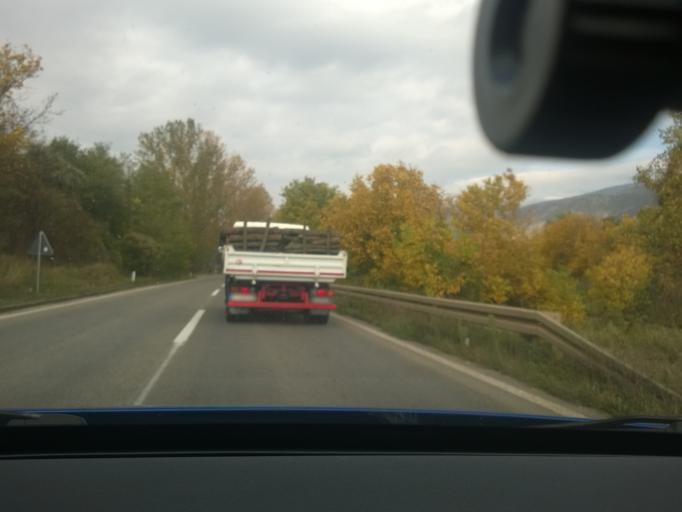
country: RS
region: Central Serbia
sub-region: Pirotski Okrug
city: Bela Palanka
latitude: 43.2792
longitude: 22.2245
